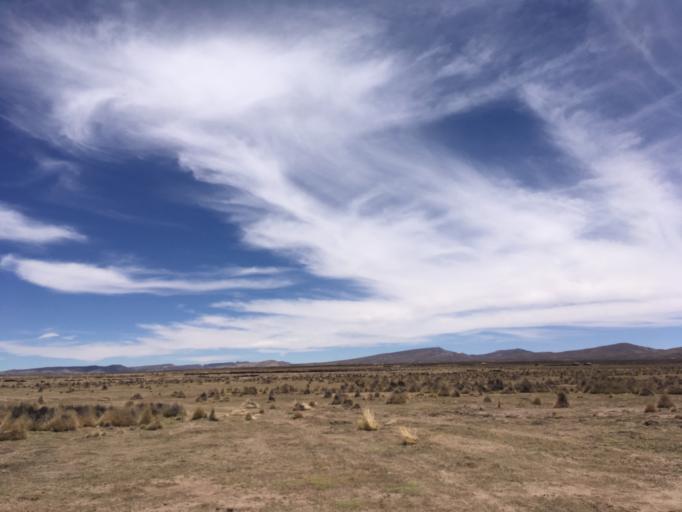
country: PE
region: Puno
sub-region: Provincia de Chucuito
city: Kelluyo
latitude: -17.0608
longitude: -69.1828
